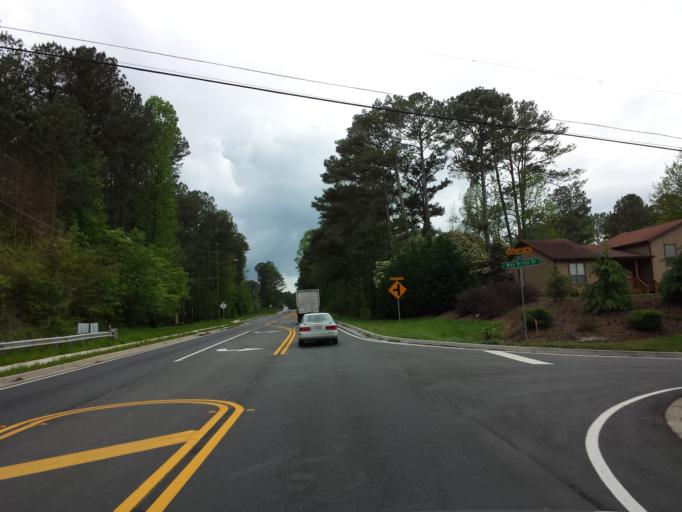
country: US
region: Georgia
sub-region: Cherokee County
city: Woodstock
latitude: 34.0684
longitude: -84.5364
